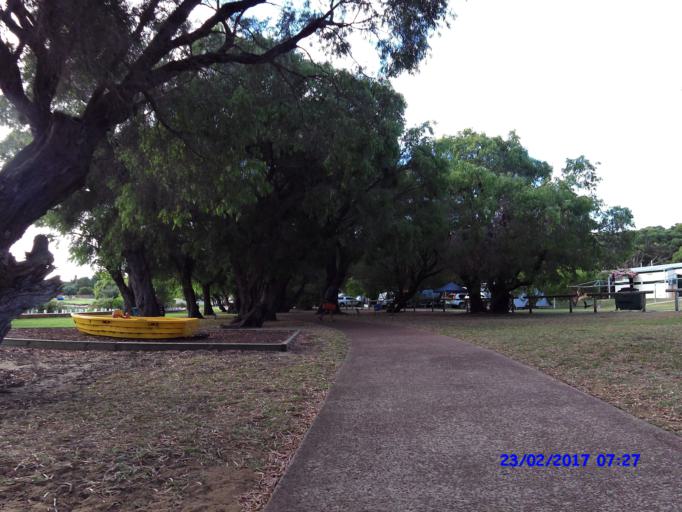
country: AU
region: Western Australia
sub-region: Augusta-Margaret River Shire
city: Augusta
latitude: -34.3238
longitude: 115.1652
